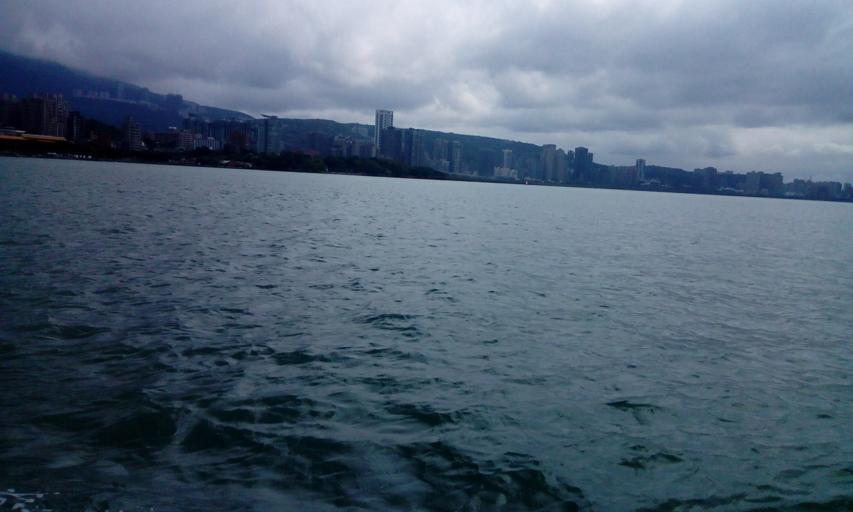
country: TW
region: Taipei
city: Taipei
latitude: 25.1673
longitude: 121.4379
